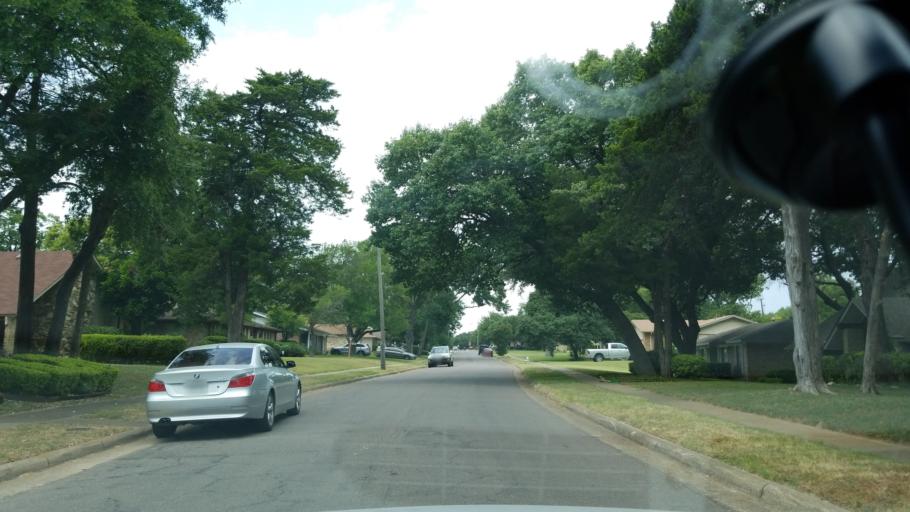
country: US
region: Texas
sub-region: Dallas County
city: Cockrell Hill
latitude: 32.6938
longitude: -96.8488
